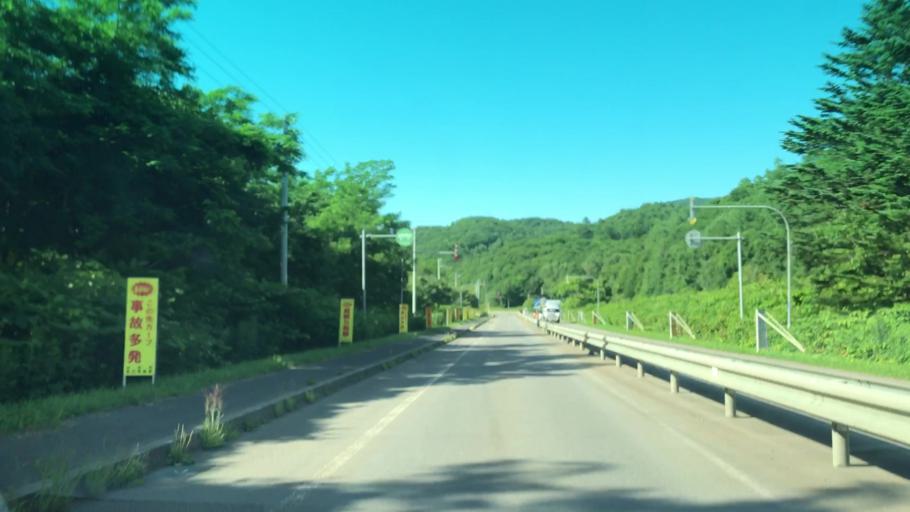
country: JP
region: Hokkaido
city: Iwanai
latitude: 42.9981
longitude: 140.6679
